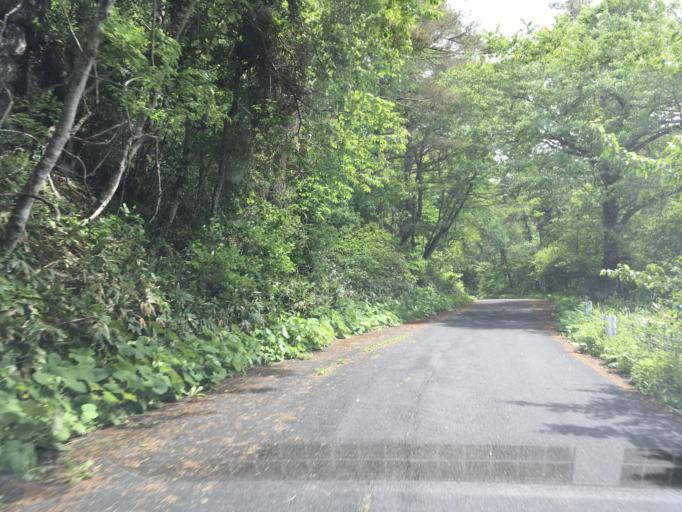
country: JP
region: Iwate
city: Mizusawa
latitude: 39.1228
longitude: 141.3010
